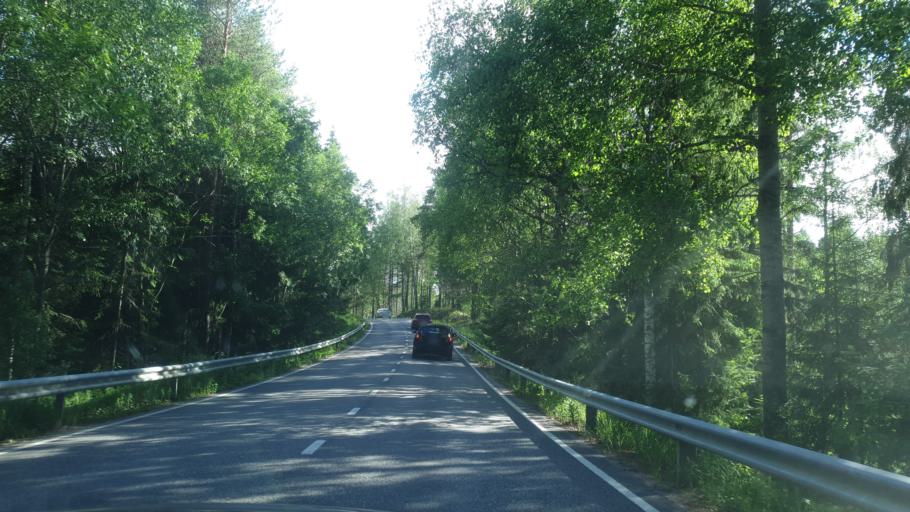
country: FI
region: Southern Savonia
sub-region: Mikkeli
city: Pertunmaa
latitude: 61.4903
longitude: 26.4721
